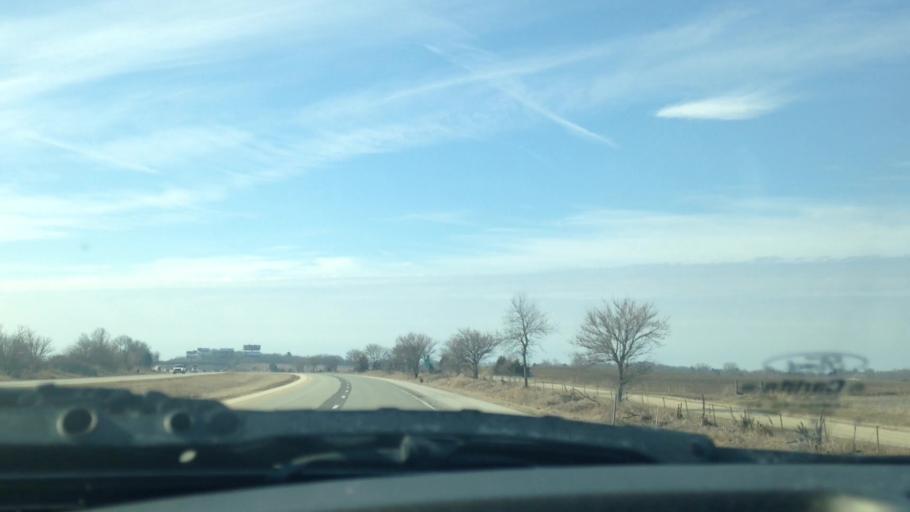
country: US
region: Illinois
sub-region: Ford County
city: Paxton
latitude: 40.5235
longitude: -88.0840
